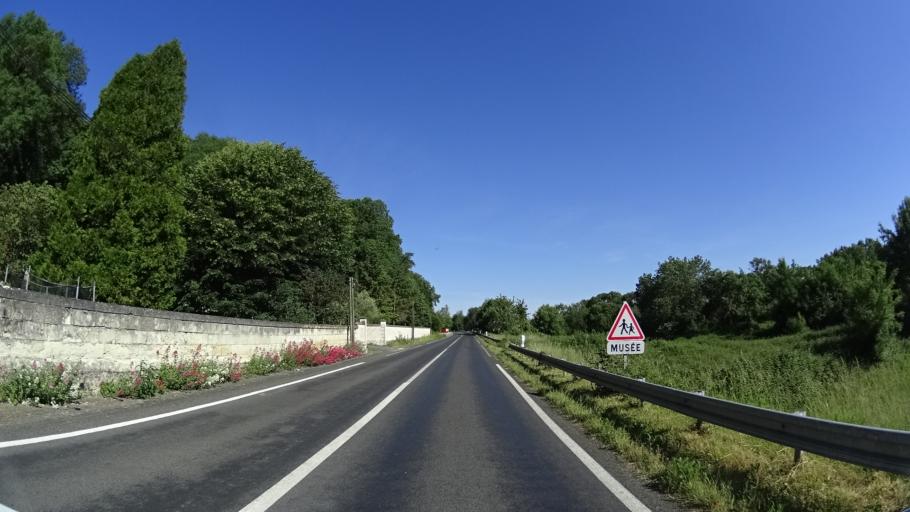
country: FR
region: Pays de la Loire
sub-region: Departement de Maine-et-Loire
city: Saumur
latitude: 47.2809
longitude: -0.1209
